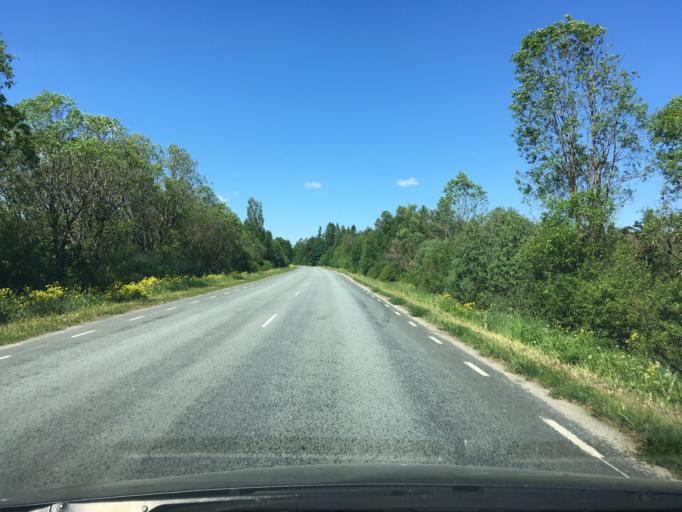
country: EE
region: Harju
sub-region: Rae vald
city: Vaida
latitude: 59.1904
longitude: 25.0031
